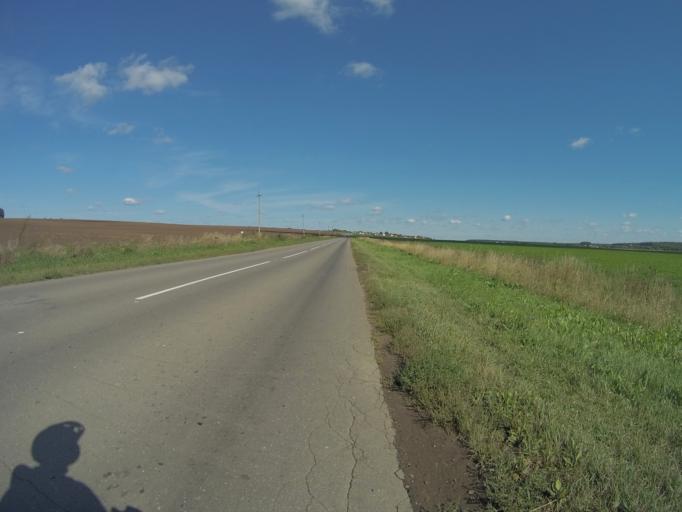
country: RU
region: Vladimir
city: Bogolyubovo
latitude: 56.2892
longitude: 40.5381
